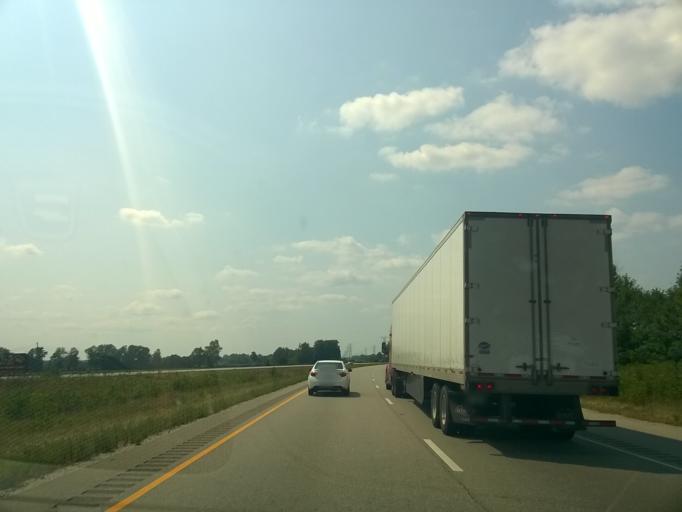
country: US
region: Indiana
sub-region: Vigo County
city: Seelyville
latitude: 39.4302
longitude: -87.3025
